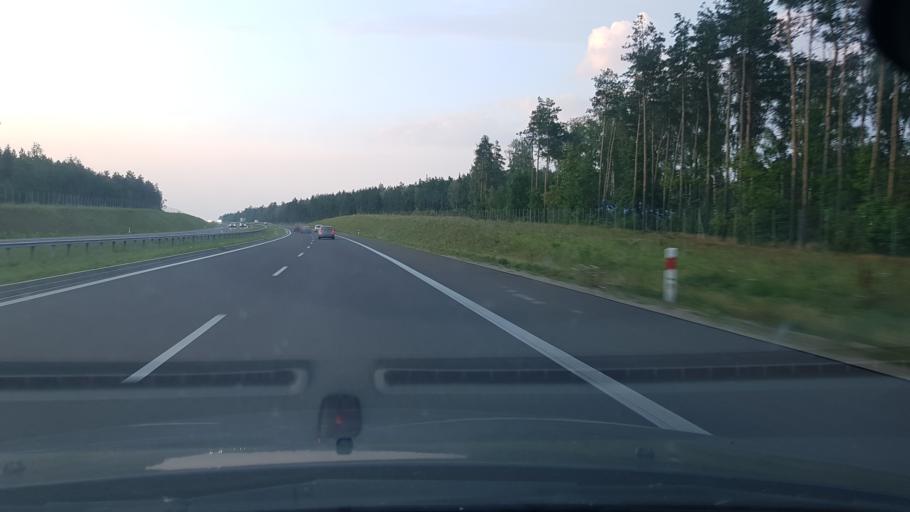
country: PL
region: Masovian Voivodeship
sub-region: Powiat mlawski
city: Wieczfnia Koscielna
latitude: 53.2393
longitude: 20.4235
